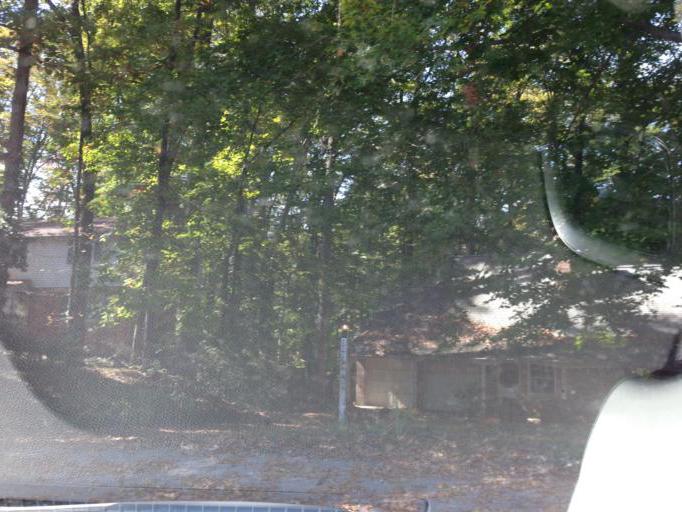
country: US
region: Maryland
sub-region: Howard County
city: Ellicott City
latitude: 39.2676
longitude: -76.8211
